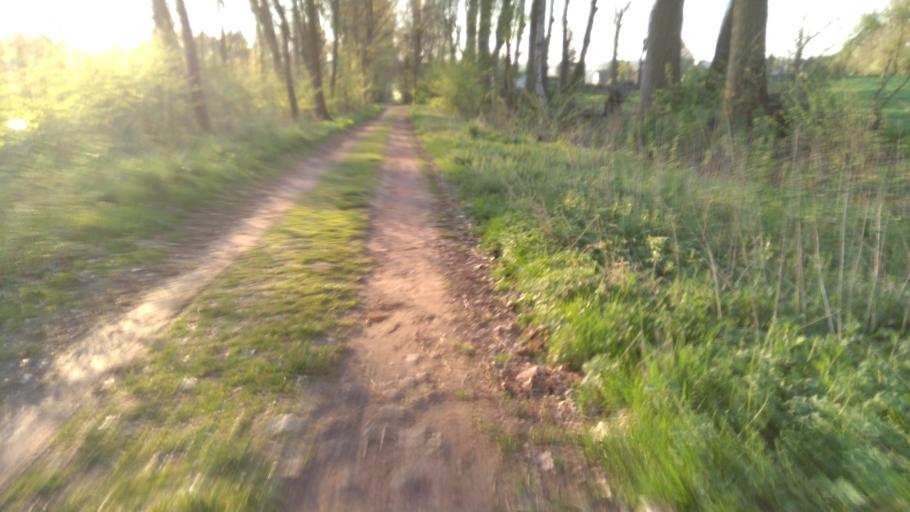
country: DE
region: Lower Saxony
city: Harsefeld
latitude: 53.4680
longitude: 9.5034
